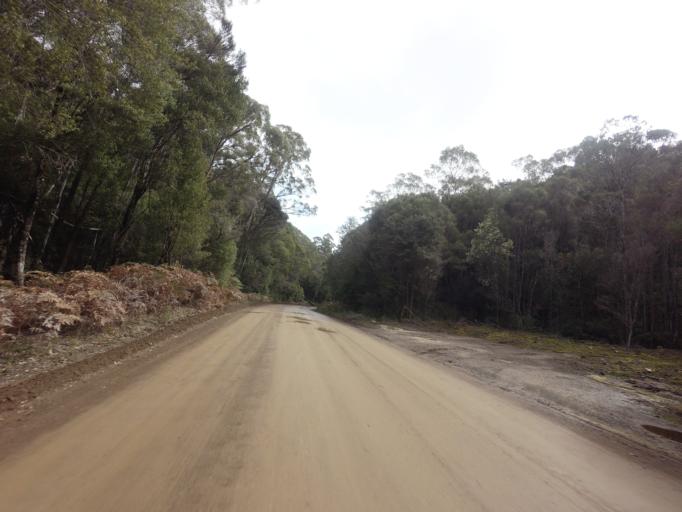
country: AU
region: Tasmania
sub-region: Huon Valley
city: Geeveston
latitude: -43.4082
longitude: 146.8708
